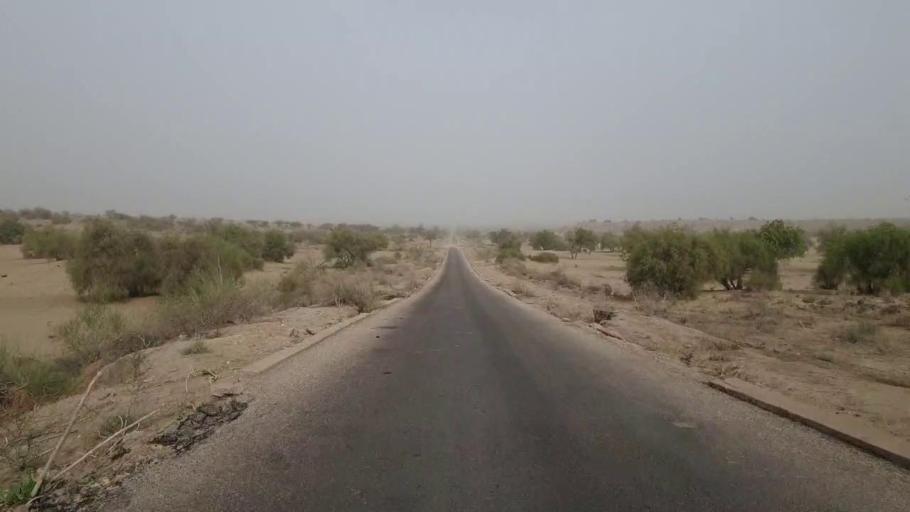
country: PK
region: Sindh
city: Islamkot
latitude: 24.5826
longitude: 70.2997
